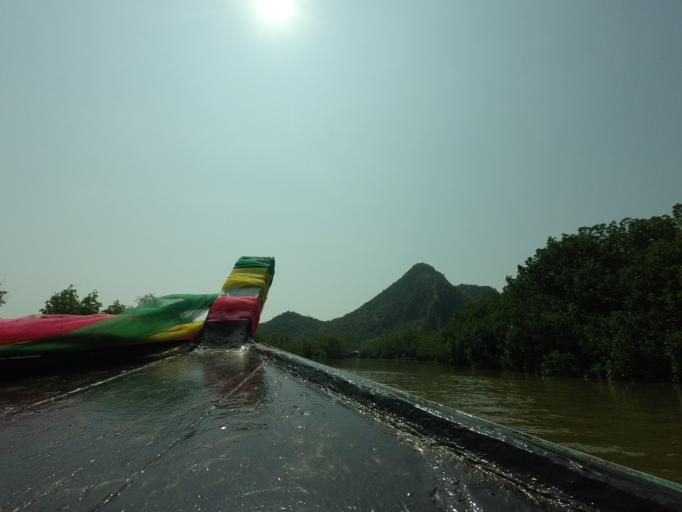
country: TH
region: Prachuap Khiri Khan
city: Kui Buri
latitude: 12.1369
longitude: 99.9612
